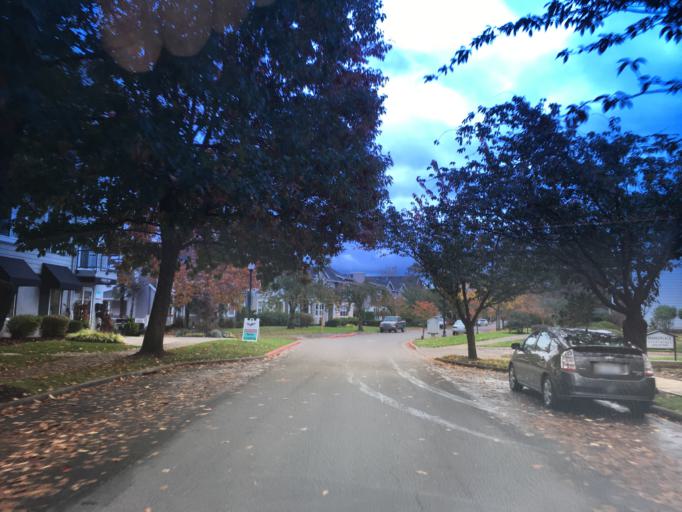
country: US
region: Oregon
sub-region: Multnomah County
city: Fairview
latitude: 45.5326
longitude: -122.4382
